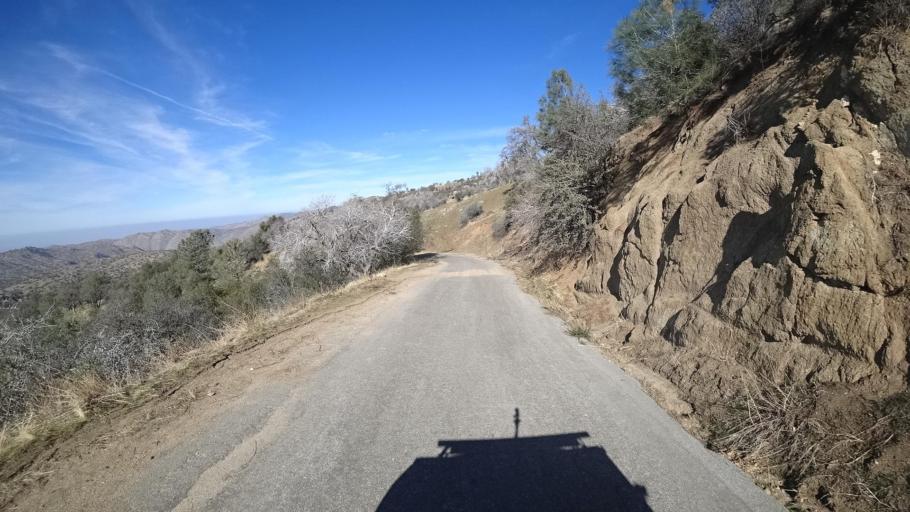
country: US
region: California
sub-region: Kern County
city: Bodfish
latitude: 35.4499
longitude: -118.6636
